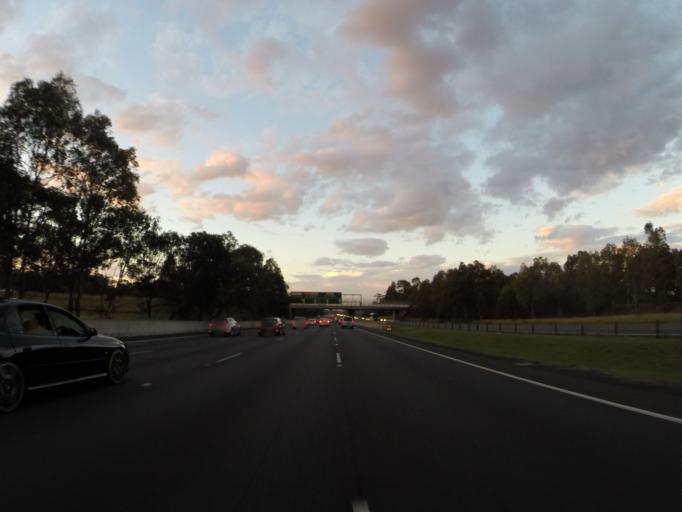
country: AU
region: New South Wales
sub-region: Campbelltown Municipality
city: Glenfield
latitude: -33.9678
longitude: 150.8745
